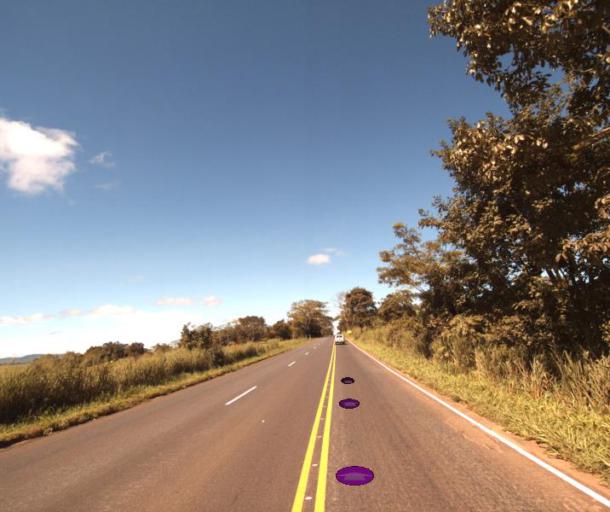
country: BR
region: Goias
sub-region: Ceres
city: Ceres
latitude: -15.1580
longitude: -49.5390
